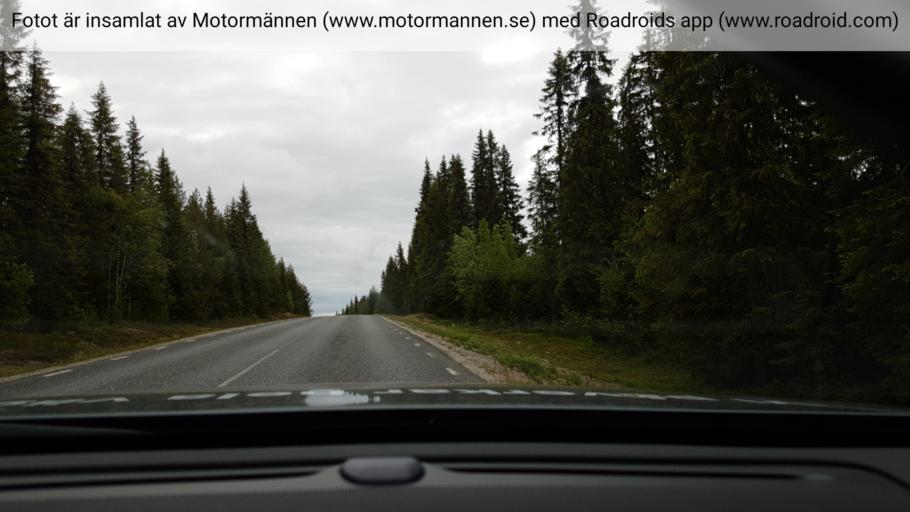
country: SE
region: Vaesterbotten
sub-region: Asele Kommun
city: Insjon
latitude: 64.3504
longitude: 17.8198
